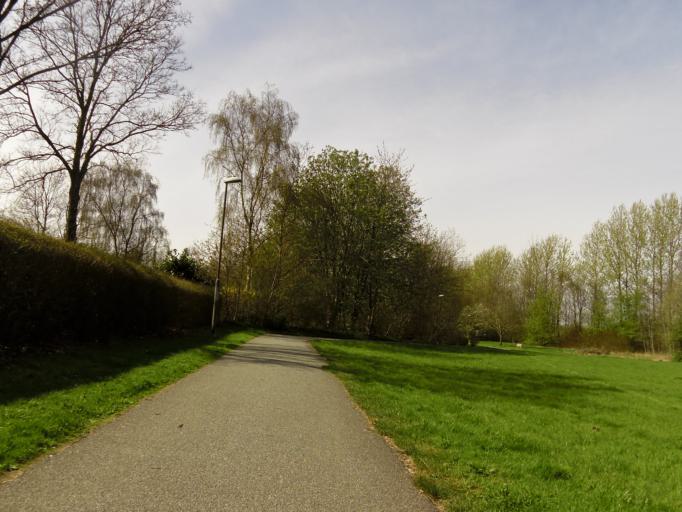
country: DK
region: Central Jutland
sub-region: Skive Kommune
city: Skive
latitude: 56.5839
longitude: 9.0217
